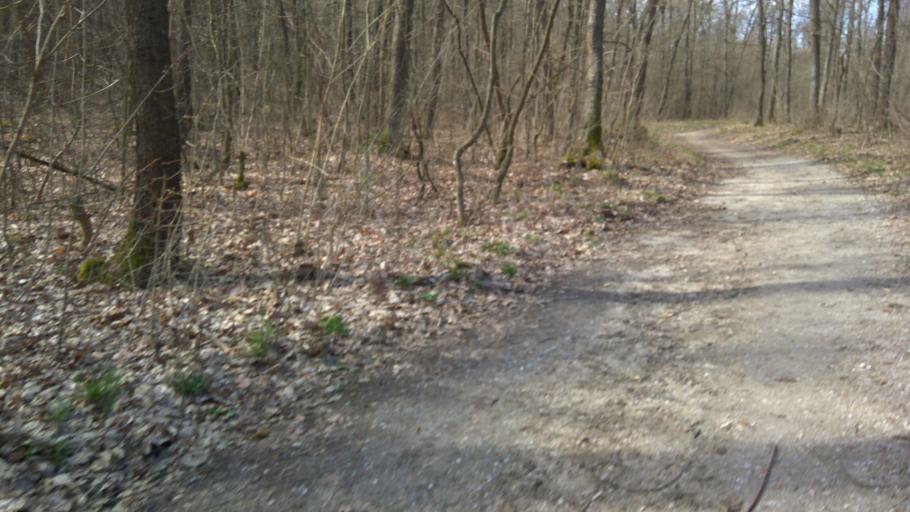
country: HU
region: Pest
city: Urom
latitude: 47.6155
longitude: 19.0113
